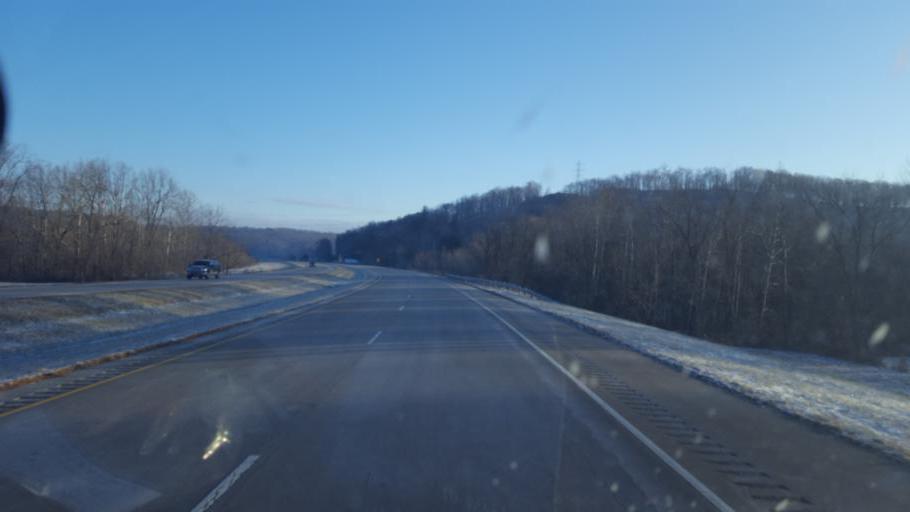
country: US
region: Ohio
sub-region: Pike County
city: Piketon
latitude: 39.0498
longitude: -83.1285
